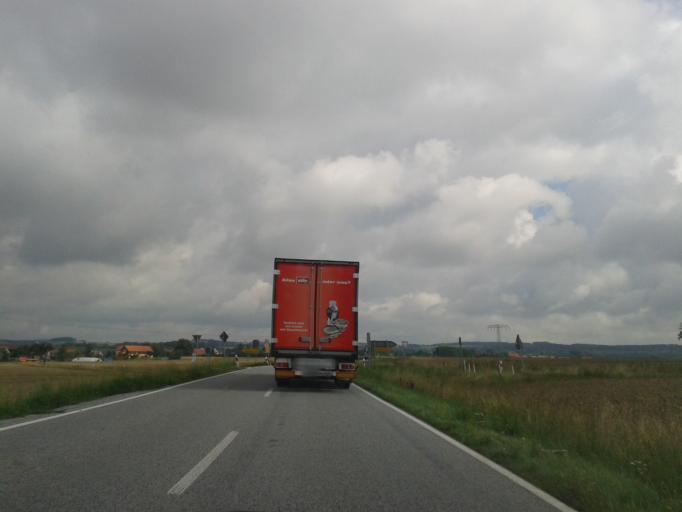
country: DE
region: Saxony
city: Lichtenberg
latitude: 51.1427
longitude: 13.9542
